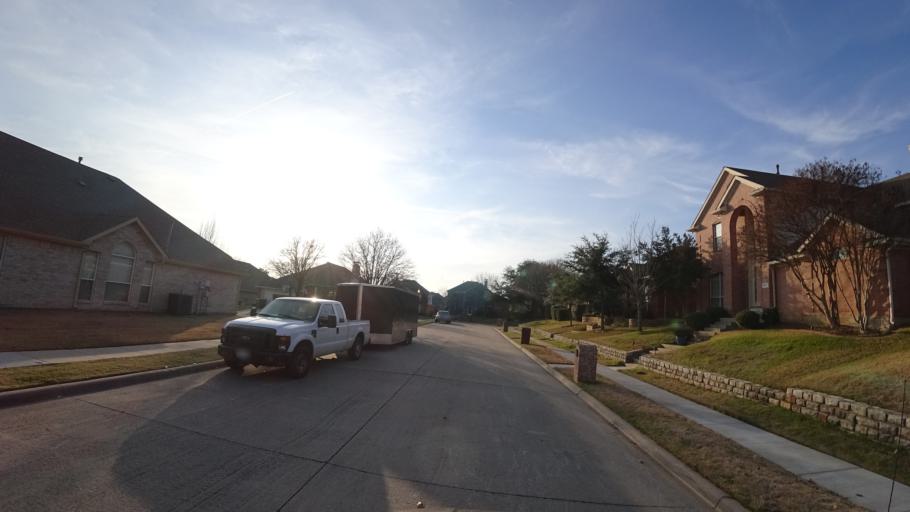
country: US
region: Texas
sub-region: Dallas County
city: Coppell
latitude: 32.9910
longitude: -96.9893
